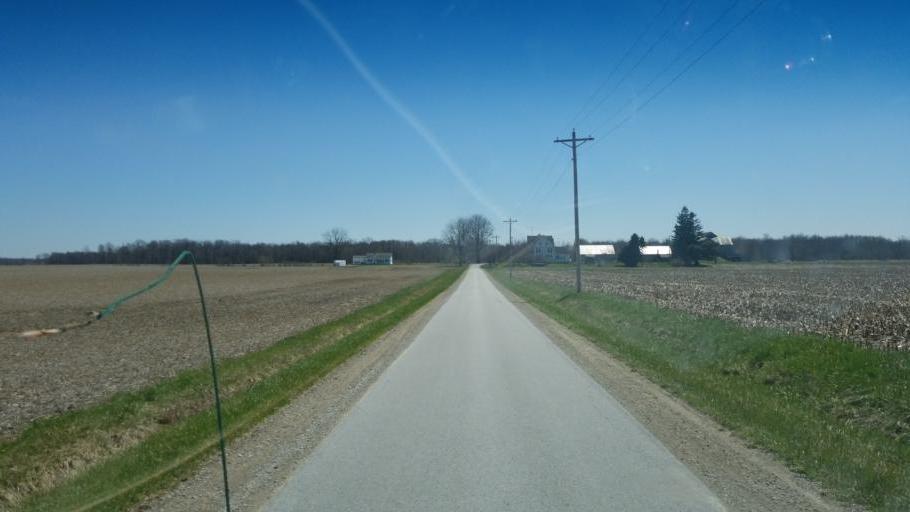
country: US
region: Ohio
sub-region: Huron County
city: Willard
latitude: 41.0474
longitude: -82.8425
